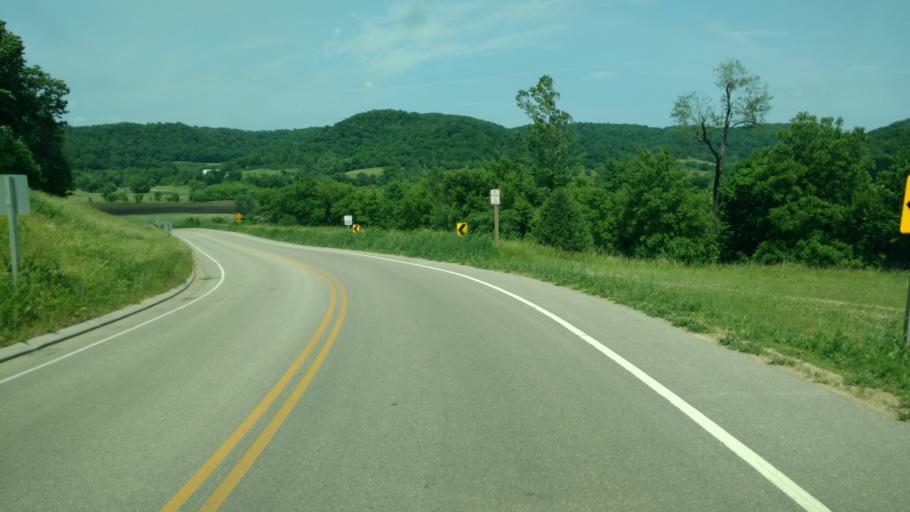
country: US
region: Wisconsin
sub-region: Vernon County
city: Viroqua
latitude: 43.5107
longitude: -90.6597
